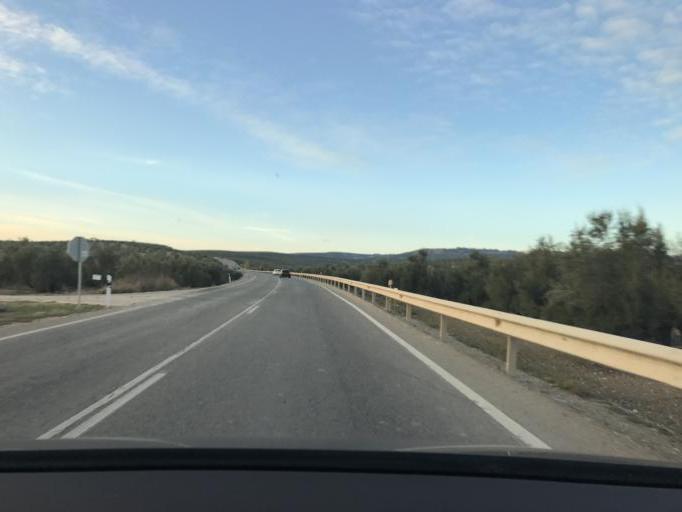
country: ES
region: Andalusia
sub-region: Provincia de Jaen
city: Ubeda
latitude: 37.9644
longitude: -3.3615
